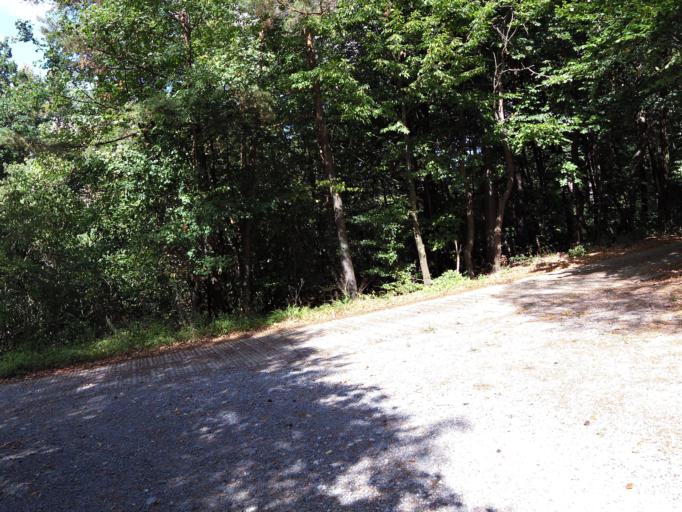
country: DE
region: Bavaria
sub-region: Regierungsbezirk Unterfranken
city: Margetshochheim
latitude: 49.8567
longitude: 9.8638
